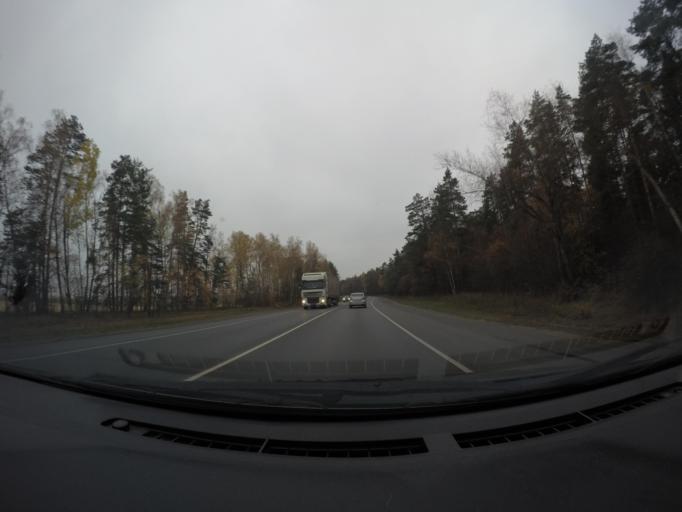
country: RU
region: Moskovskaya
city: Malyshevo
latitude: 55.4458
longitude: 38.3212
